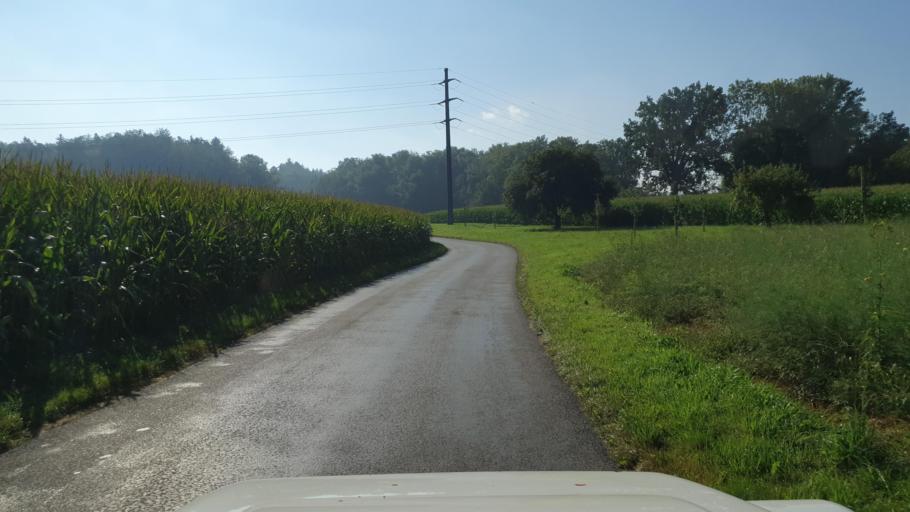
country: CH
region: Aargau
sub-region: Bezirk Bremgarten
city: Villmergen
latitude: 47.3403
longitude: 8.2502
